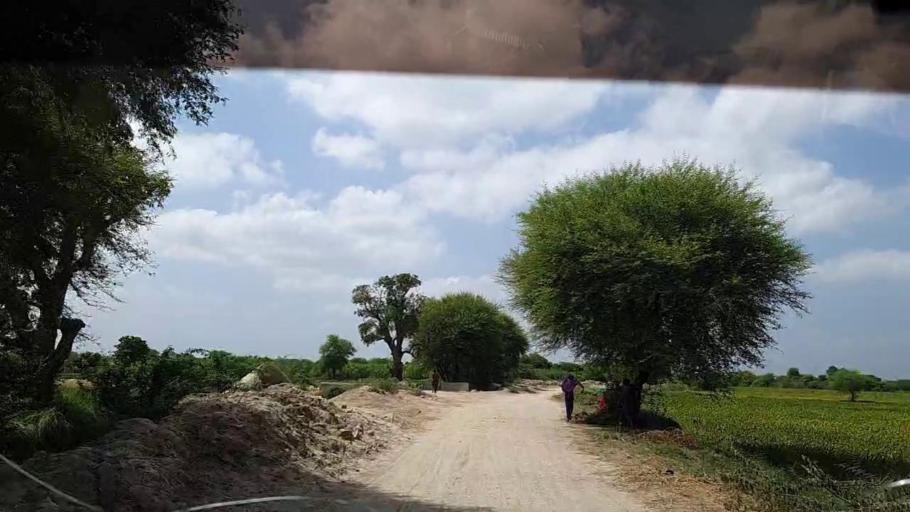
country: PK
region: Sindh
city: Badin
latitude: 24.5964
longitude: 68.7780
